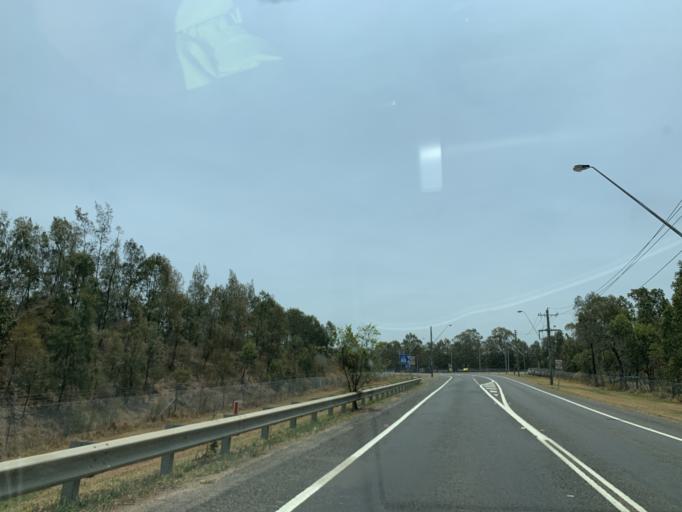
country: AU
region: New South Wales
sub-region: Fairfield
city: Horsley Park
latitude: -33.8187
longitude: 150.8674
